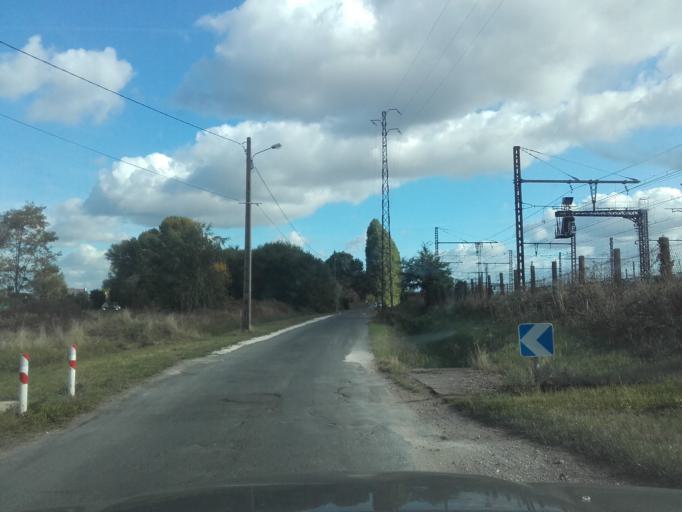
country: FR
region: Centre
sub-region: Departement d'Indre-et-Loire
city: La Ville-aux-Dames
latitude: 47.3930
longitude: 0.7578
